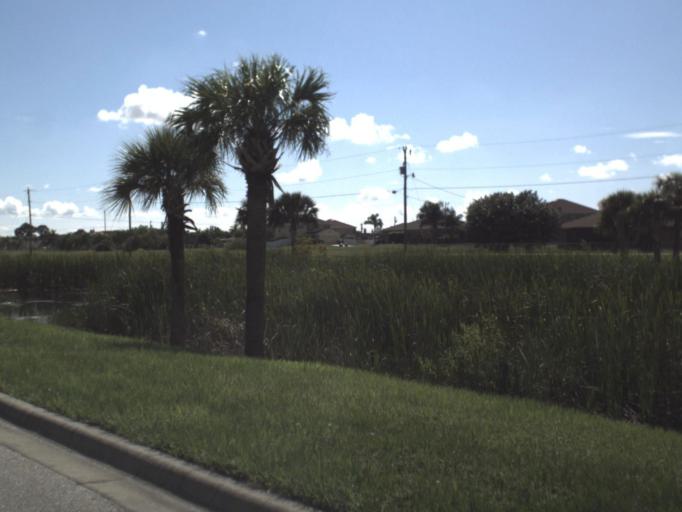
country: US
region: Florida
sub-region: Lee County
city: Lochmoor Waterway Estates
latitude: 26.6711
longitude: -81.9416
